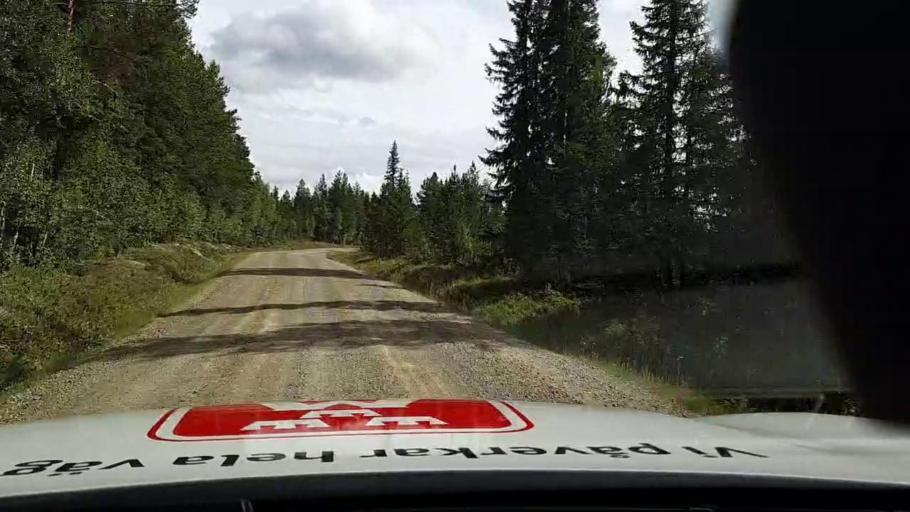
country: SE
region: Jaemtland
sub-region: Are Kommun
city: Jarpen
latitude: 62.5450
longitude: 13.4723
